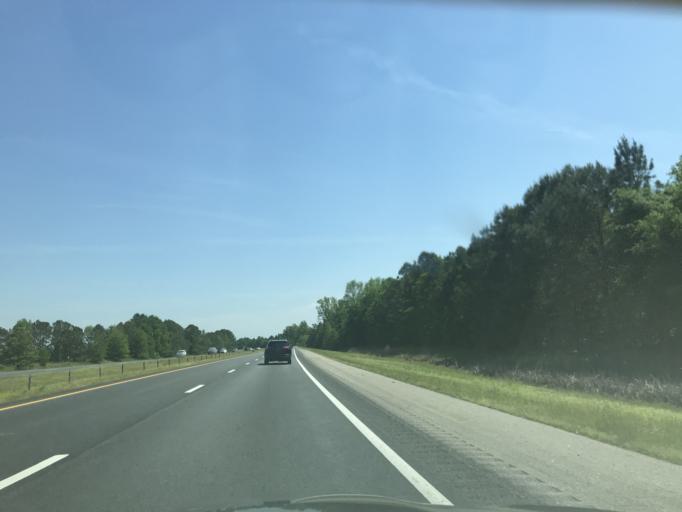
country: US
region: North Carolina
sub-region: Johnston County
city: Benson
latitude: 35.3382
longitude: -78.4630
